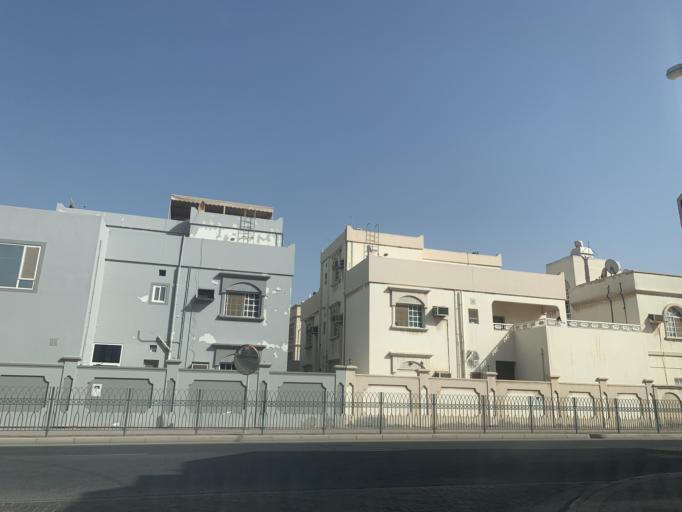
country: BH
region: Northern
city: Madinat `Isa
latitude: 26.1623
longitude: 50.5755
